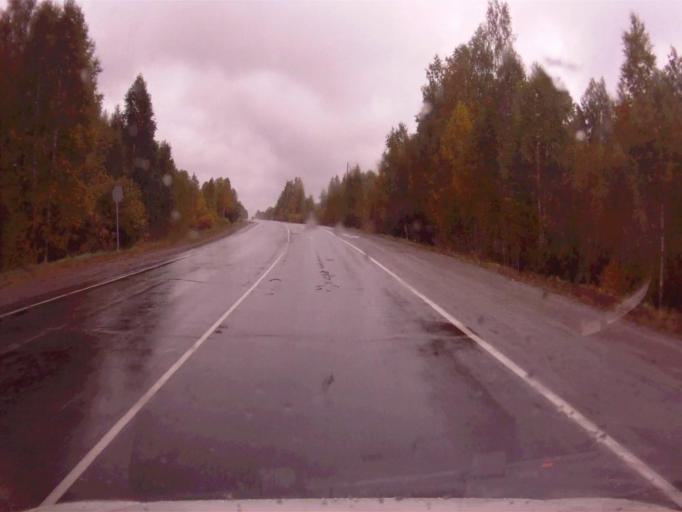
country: RU
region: Chelyabinsk
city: Argayash
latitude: 55.4866
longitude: 60.7351
